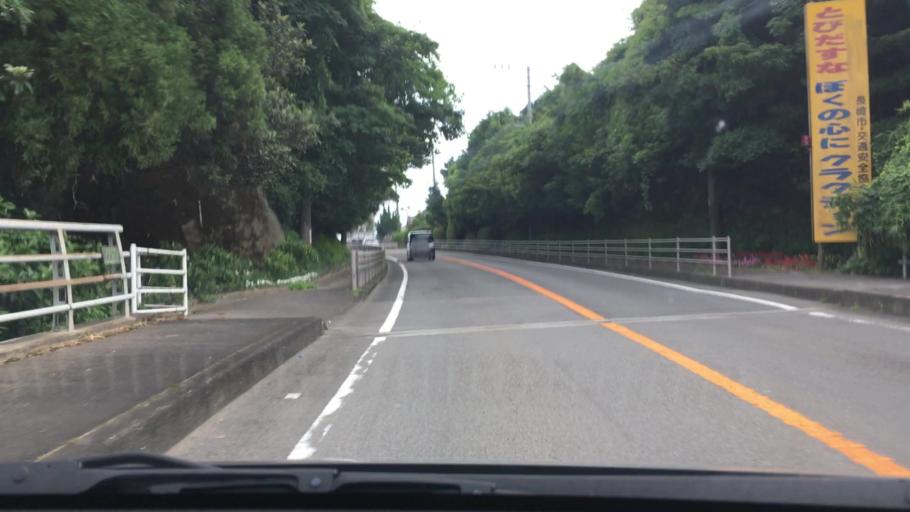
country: JP
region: Nagasaki
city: Togitsu
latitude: 32.9024
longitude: 129.7802
